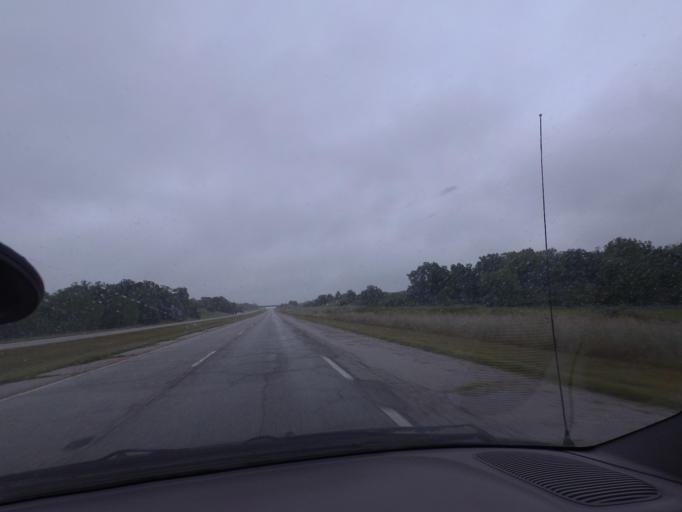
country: US
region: Illinois
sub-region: Pike County
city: Barry
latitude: 39.6903
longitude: -90.9236
